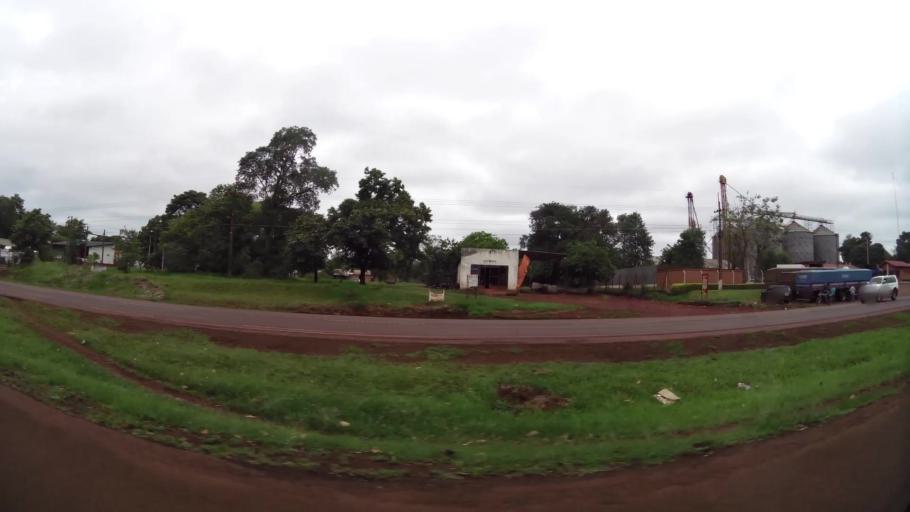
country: PY
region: Alto Parana
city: Colonia Yguazu
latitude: -25.4888
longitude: -54.8107
